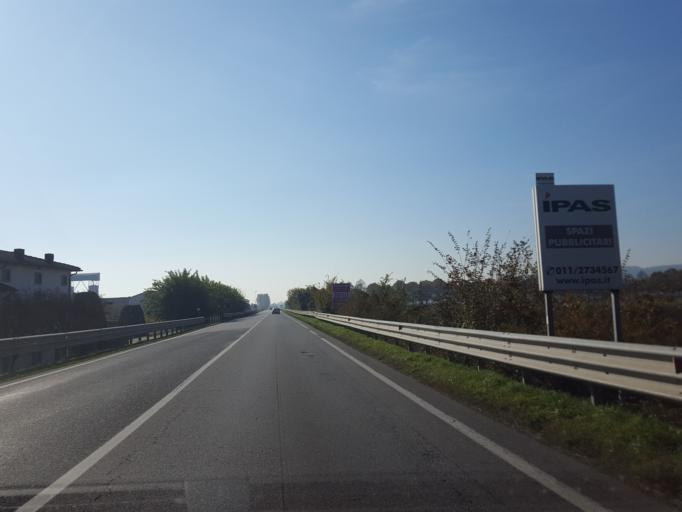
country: IT
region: Veneto
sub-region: Provincia di Vicenza
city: Brendola
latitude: 45.4787
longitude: 11.4157
